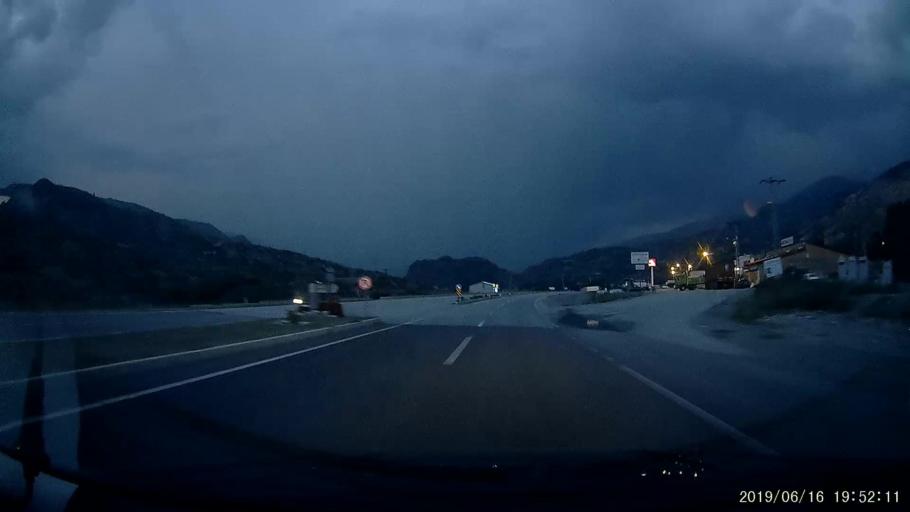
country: TR
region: Sivas
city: Koyulhisar
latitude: 40.2854
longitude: 37.8075
